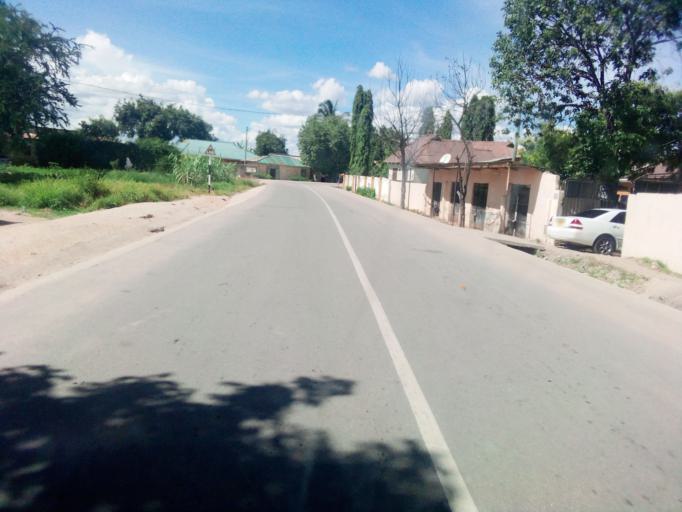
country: TZ
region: Dodoma
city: Dodoma
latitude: -6.1723
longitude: 35.7596
